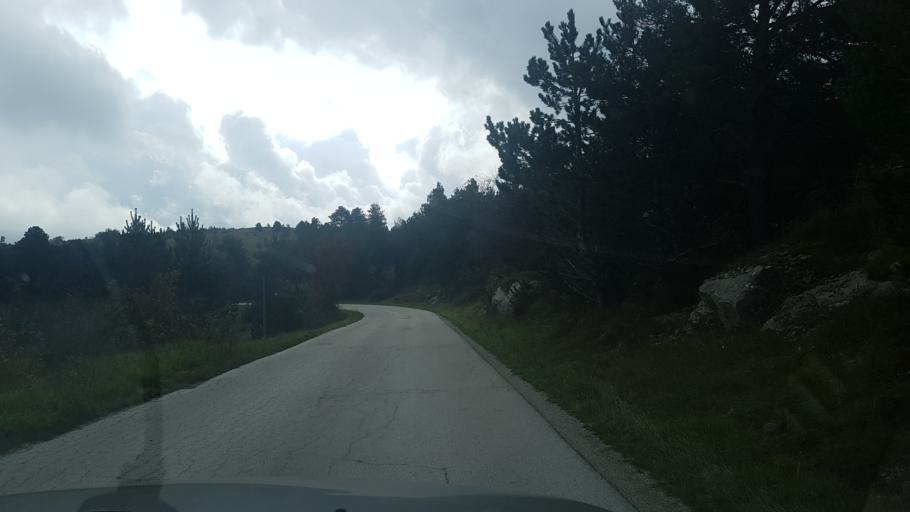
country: HR
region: Istarska
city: Buzet
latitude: 45.4991
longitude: 14.0118
